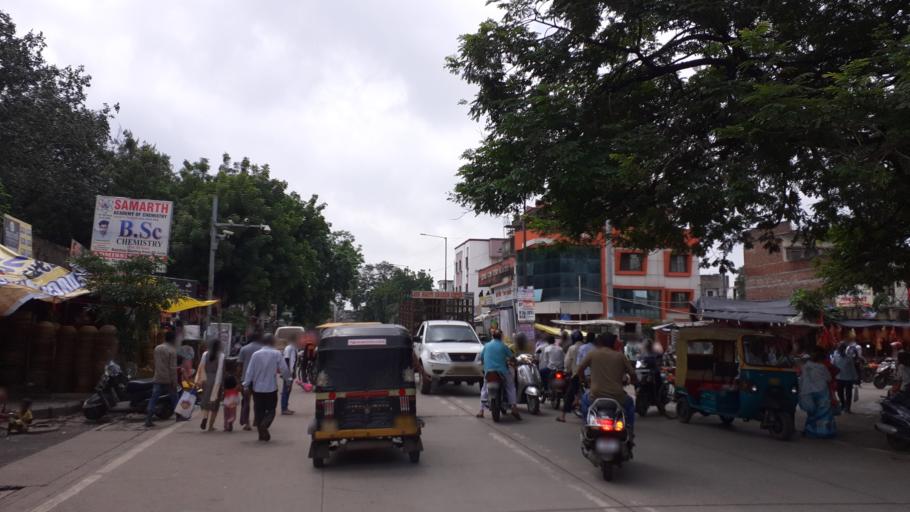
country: IN
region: Maharashtra
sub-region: Nagpur Division
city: Nagpur
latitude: 21.1273
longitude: 79.1131
